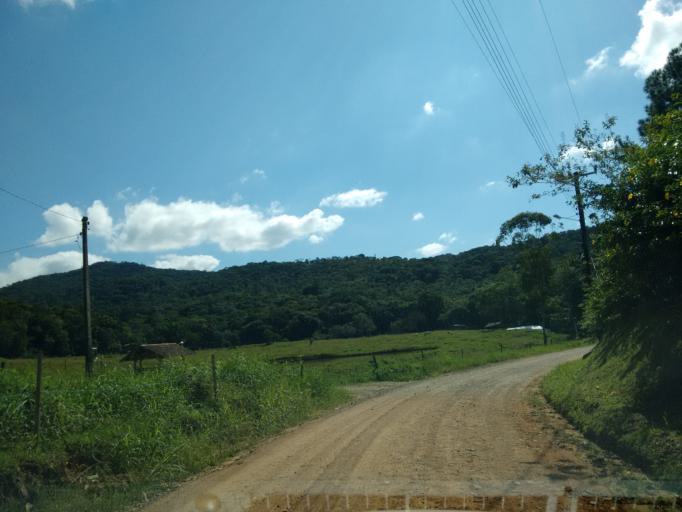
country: BR
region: Santa Catarina
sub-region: Indaial
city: Indaial
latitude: -26.9763
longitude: -49.1757
